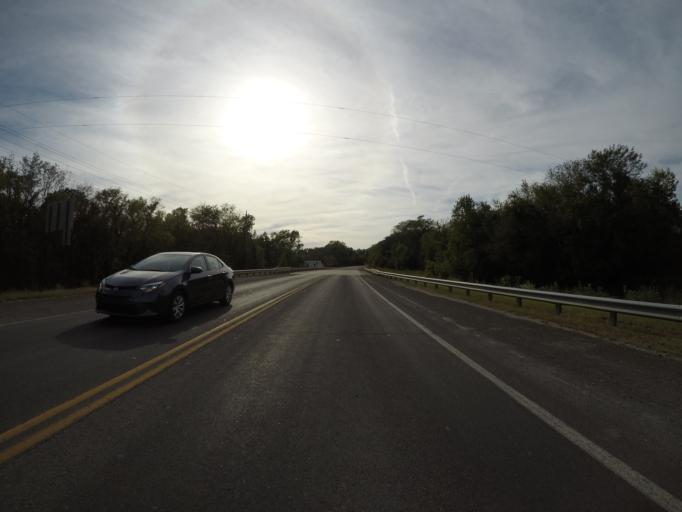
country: US
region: Kansas
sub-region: Johnson County
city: Edgerton
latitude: 38.7681
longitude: -95.0046
